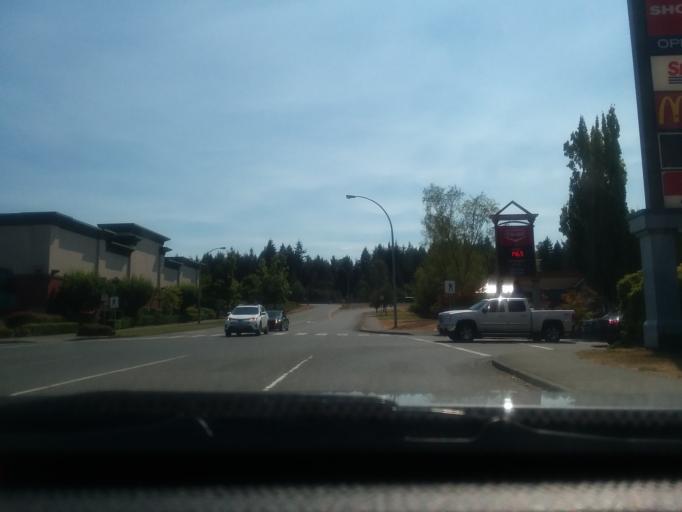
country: CA
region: British Columbia
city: Nanaimo
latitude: 49.2390
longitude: -124.0548
